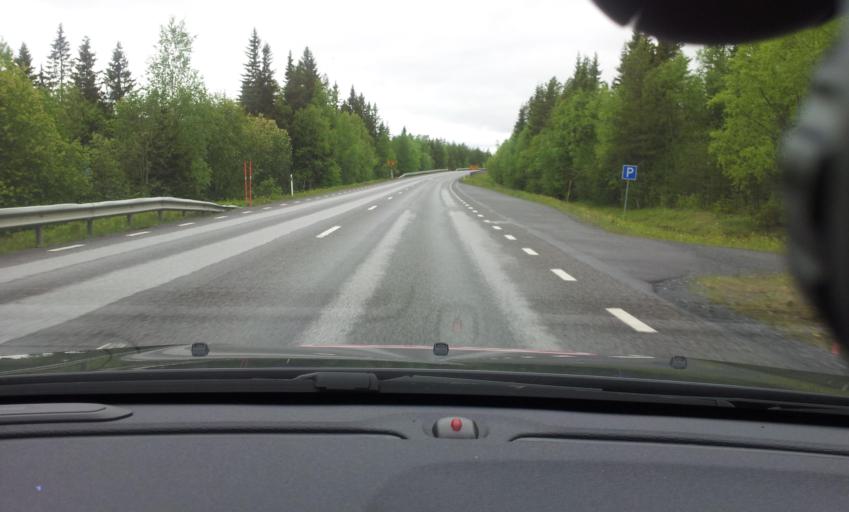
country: SE
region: Jaemtland
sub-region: Krokoms Kommun
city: Valla
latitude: 63.3060
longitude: 13.8441
